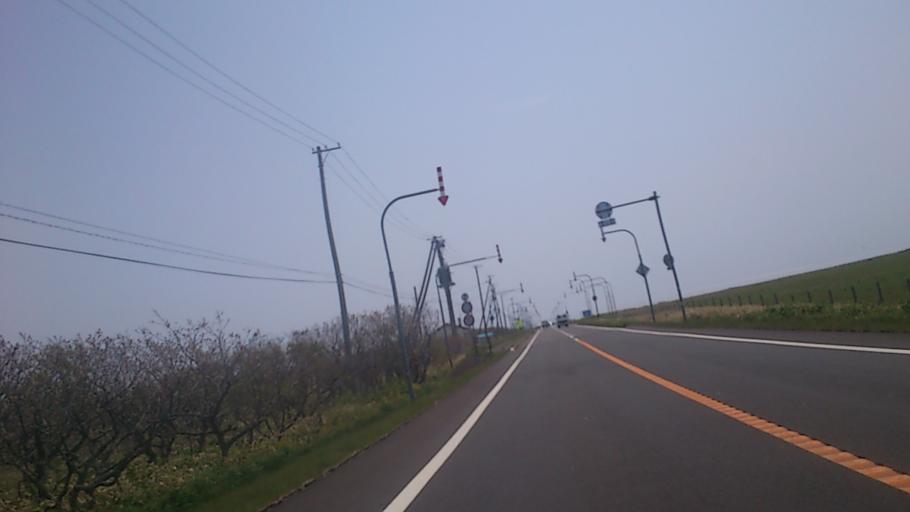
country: JP
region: Hokkaido
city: Nemuro
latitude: 43.3898
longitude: 145.7548
